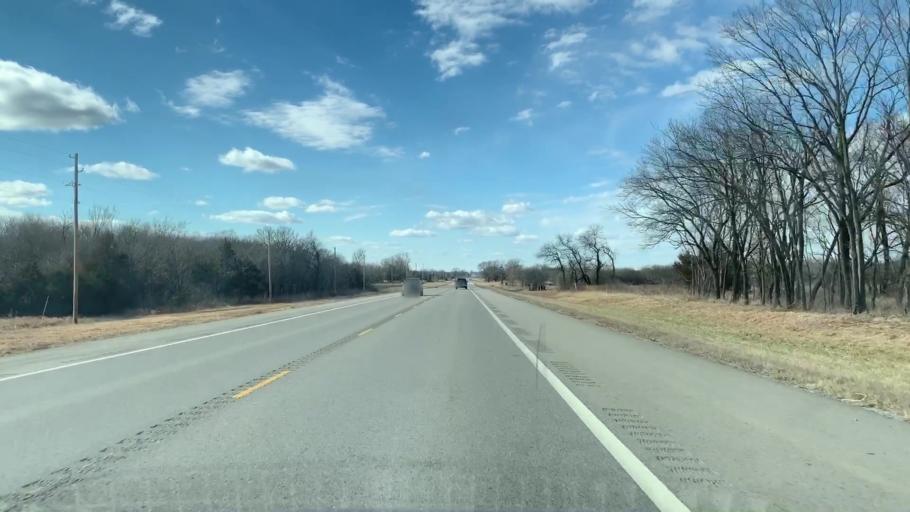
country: US
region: Kansas
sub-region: Labette County
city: Oswego
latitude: 37.3401
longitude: -95.0612
